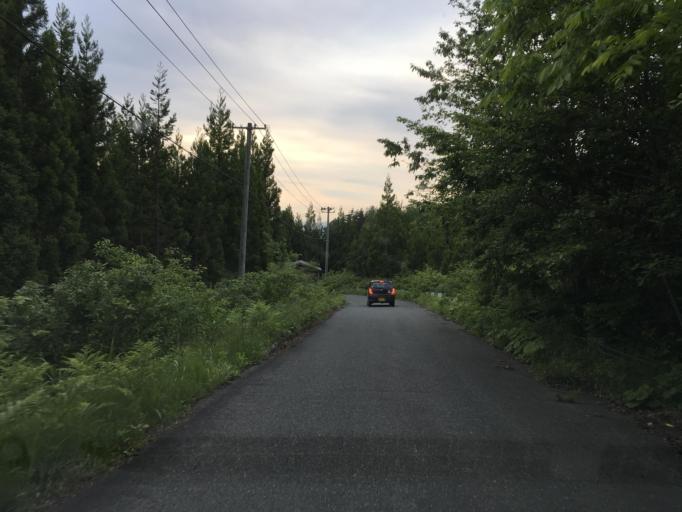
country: JP
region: Iwate
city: Mizusawa
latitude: 39.1499
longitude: 141.2991
